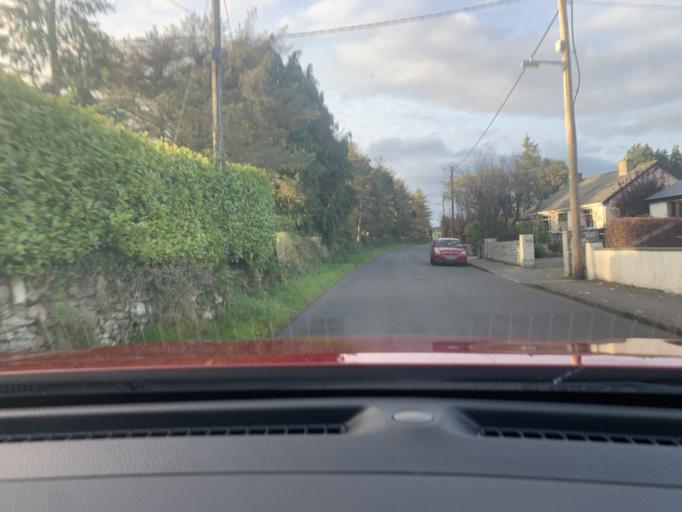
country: IE
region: Connaught
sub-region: Roscommon
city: Ballaghaderreen
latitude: 53.9053
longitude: -8.5772
